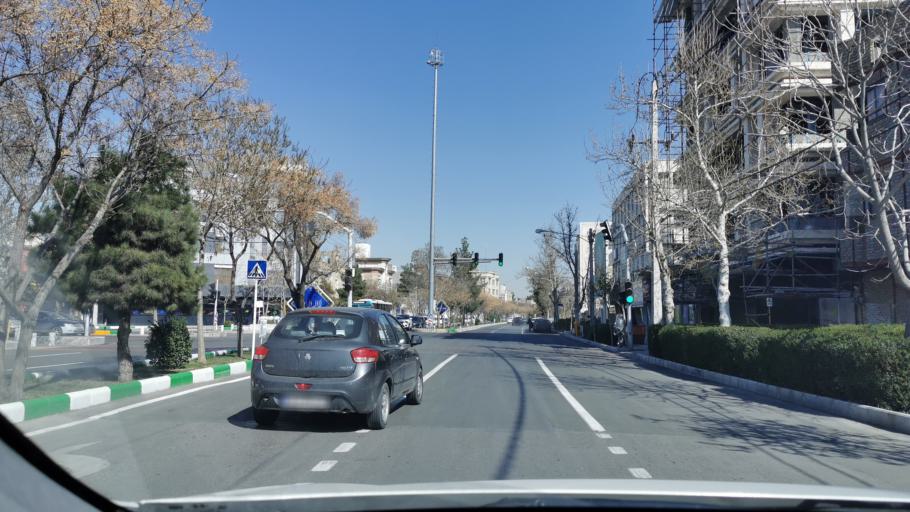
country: IR
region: Razavi Khorasan
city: Mashhad
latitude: 36.2918
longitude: 59.5722
